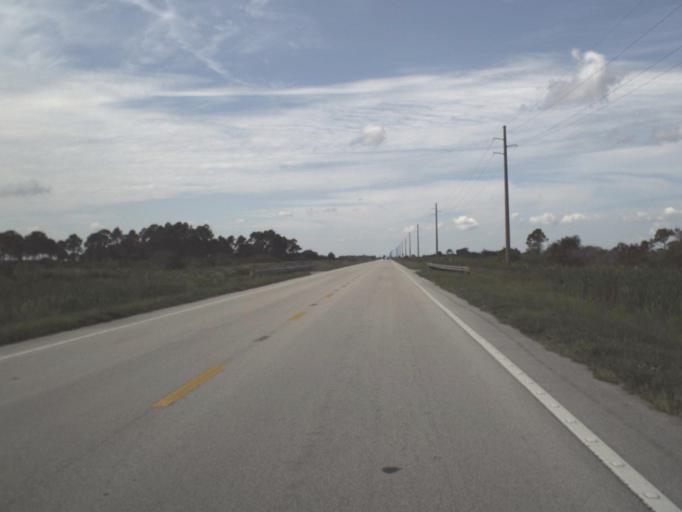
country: US
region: Florida
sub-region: Highlands County
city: Placid Lakes
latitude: 27.2090
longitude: -81.5011
